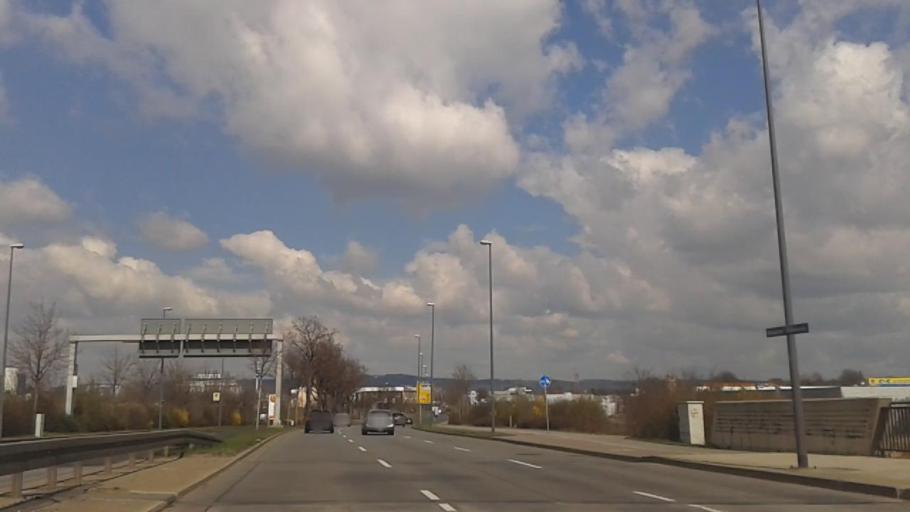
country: DE
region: Saxony
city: Radebeul
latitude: 51.0657
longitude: 13.6896
